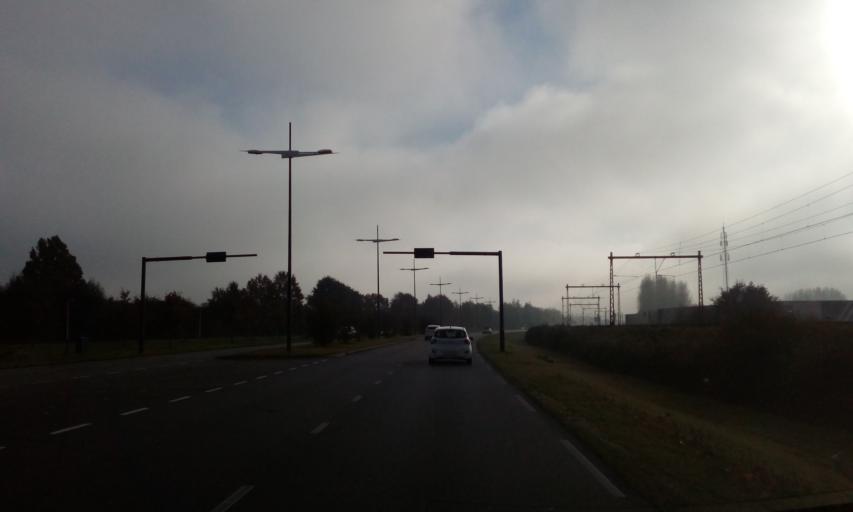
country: NL
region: Gelderland
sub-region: Gemeente Lochem
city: Epse
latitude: 52.2443
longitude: 6.2059
